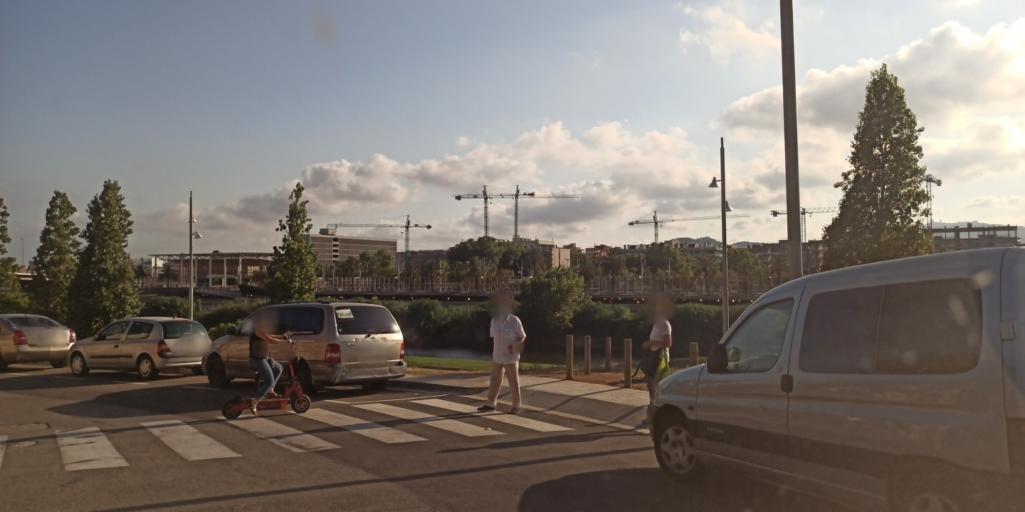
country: ES
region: Catalonia
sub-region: Provincia de Barcelona
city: Llefia
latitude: 41.4392
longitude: 2.2106
